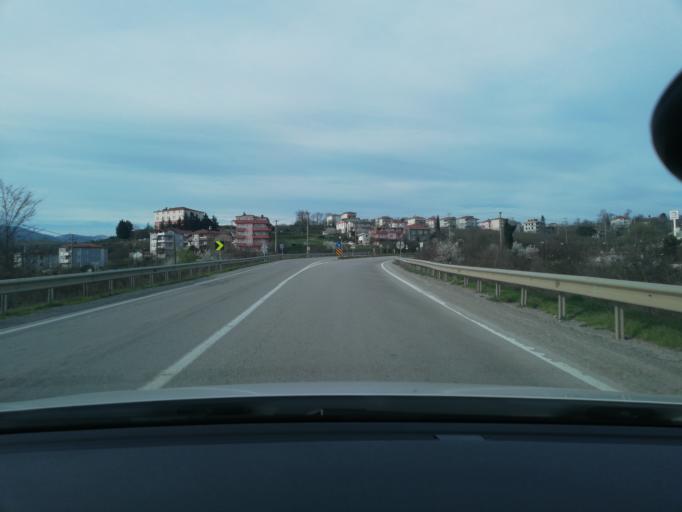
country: TR
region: Duzce
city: Akcakoca
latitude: 41.0838
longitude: 31.1473
